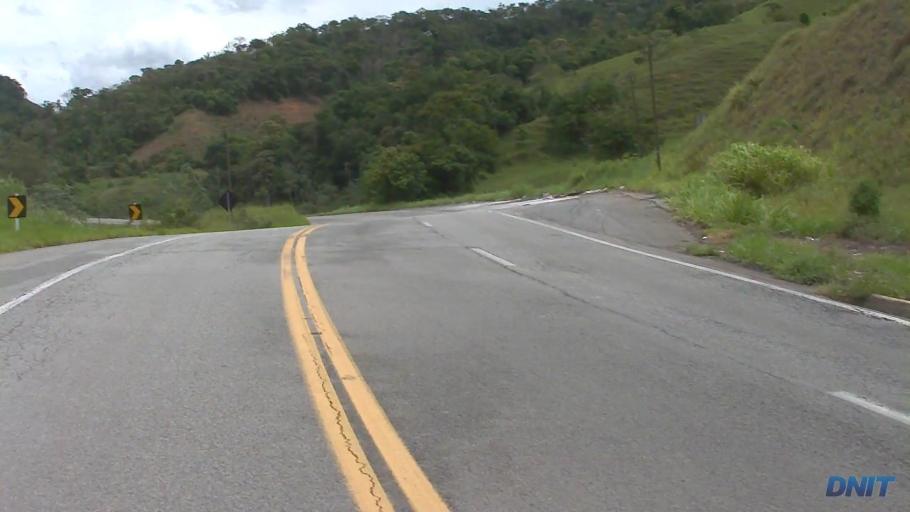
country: BR
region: Minas Gerais
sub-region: Nova Era
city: Nova Era
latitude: -19.6308
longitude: -42.8745
